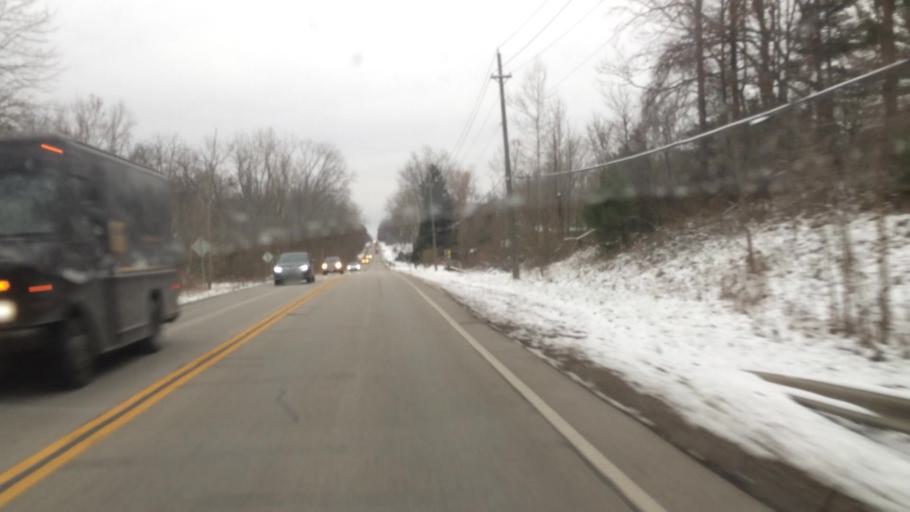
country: US
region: Ohio
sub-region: Cuyahoga County
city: Strongsville
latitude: 41.3089
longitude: -81.7854
